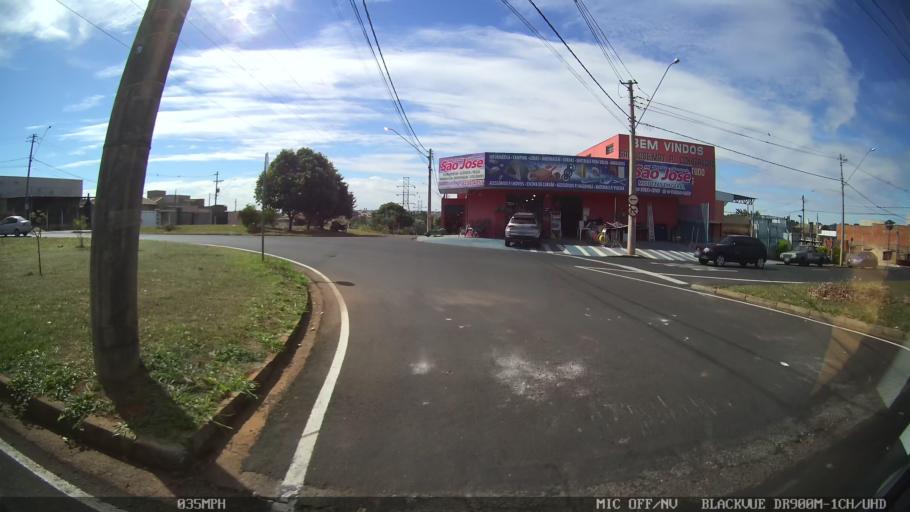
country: BR
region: Sao Paulo
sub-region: Sao Jose Do Rio Preto
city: Sao Jose do Rio Preto
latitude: -20.8334
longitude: -49.3488
